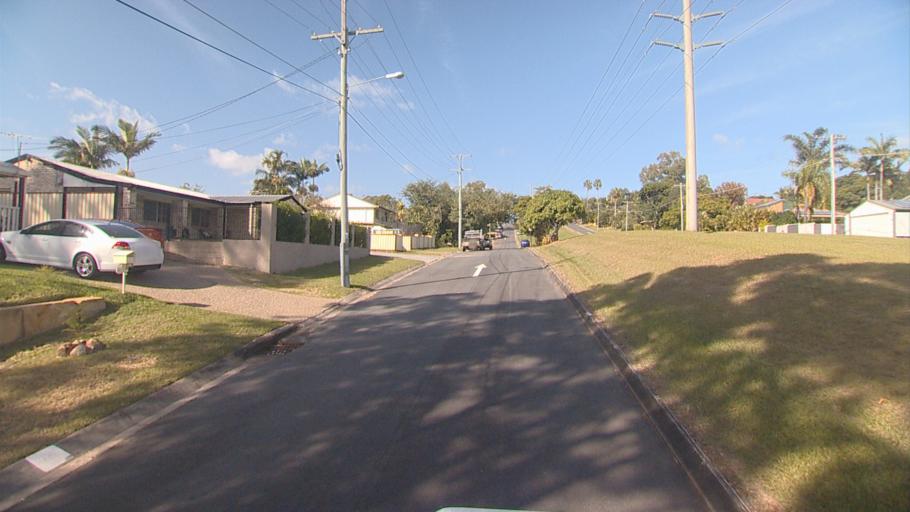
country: AU
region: Queensland
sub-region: Logan
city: Beenleigh
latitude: -27.7061
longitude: 153.1788
